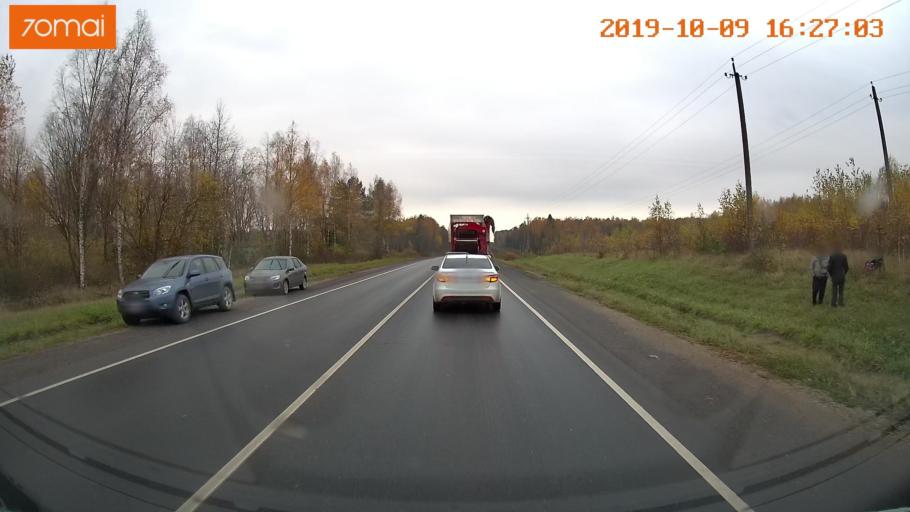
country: RU
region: Kostroma
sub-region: Kostromskoy Rayon
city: Kostroma
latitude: 57.6348
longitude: 40.9267
